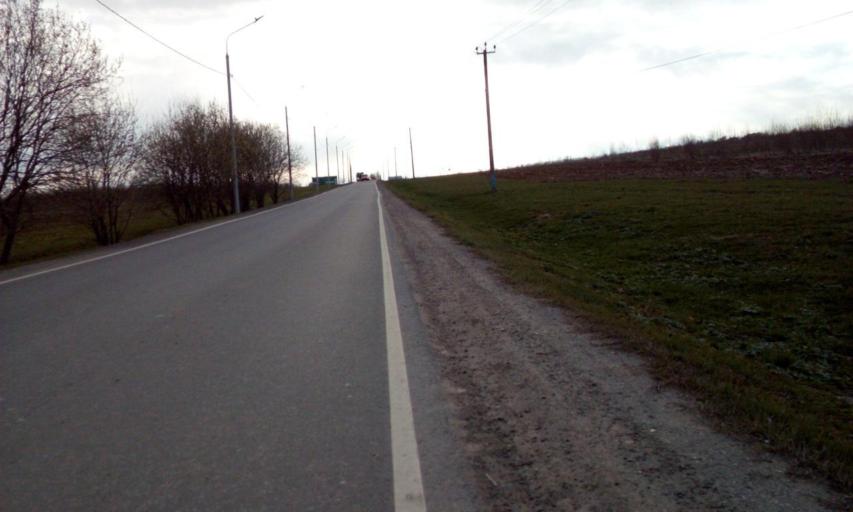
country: RU
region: Moskovskaya
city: Annino
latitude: 55.5230
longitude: 37.2488
